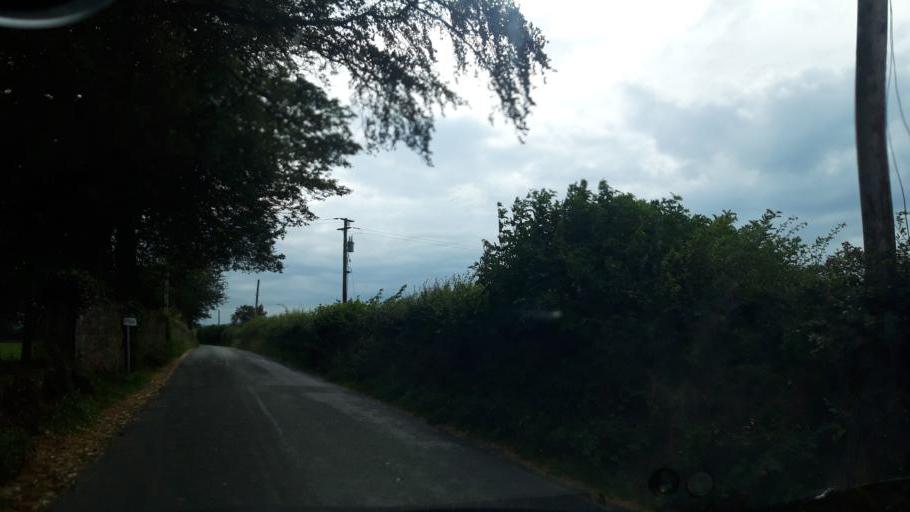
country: IE
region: Leinster
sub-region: Kilkenny
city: Ballyragget
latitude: 52.7587
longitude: -7.3792
